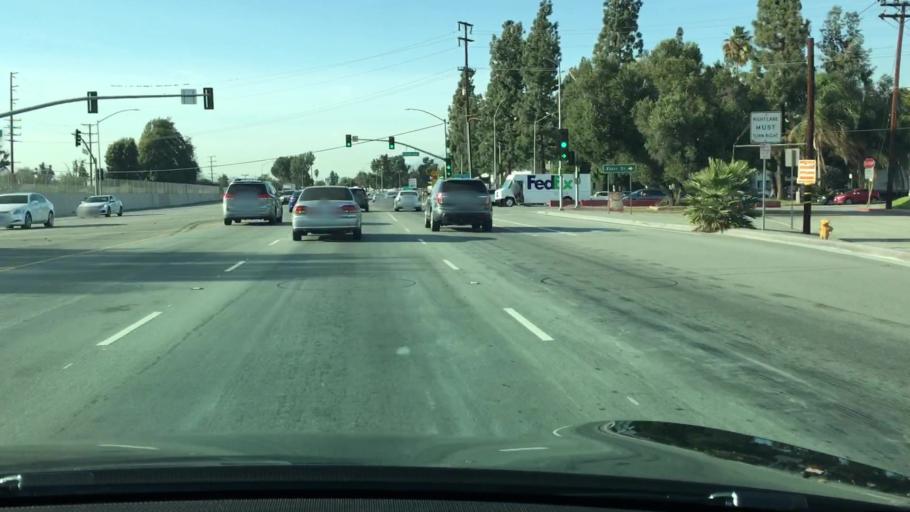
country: US
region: California
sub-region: Los Angeles County
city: Rosemead
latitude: 34.0678
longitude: -118.0702
